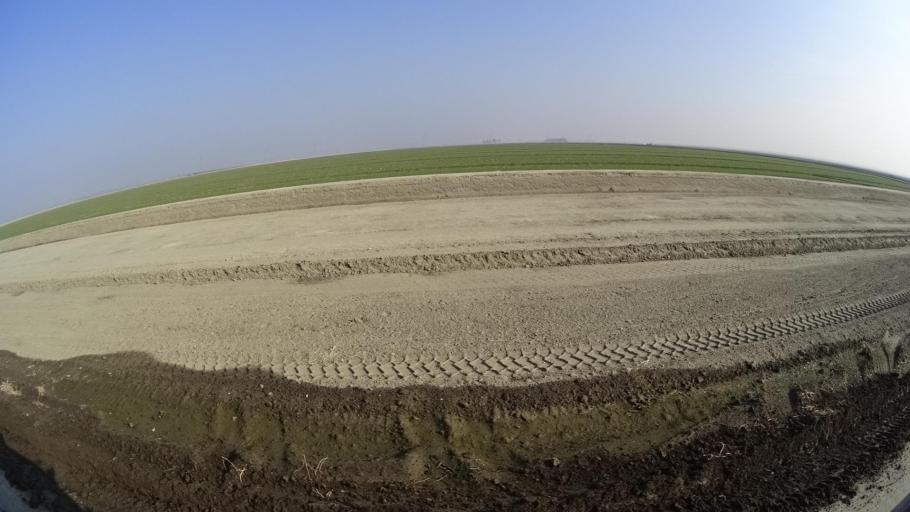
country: US
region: California
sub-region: Kern County
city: Greenfield
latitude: 35.1530
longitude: -119.0392
